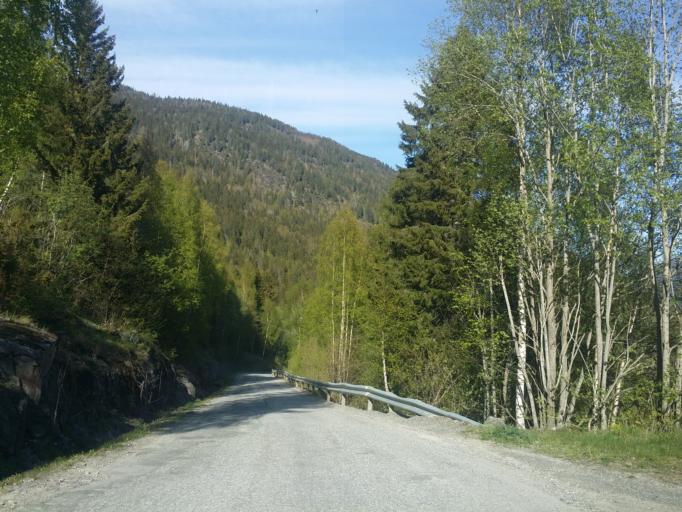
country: NO
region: Telemark
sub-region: Seljord
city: Seljord
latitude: 59.6080
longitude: 8.6868
